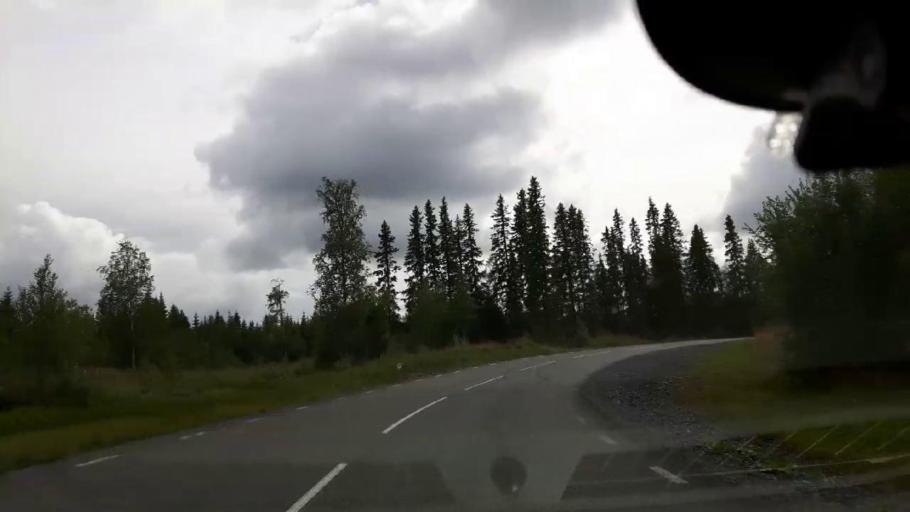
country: SE
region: Jaemtland
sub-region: Krokoms Kommun
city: Valla
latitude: 63.4816
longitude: 13.8581
